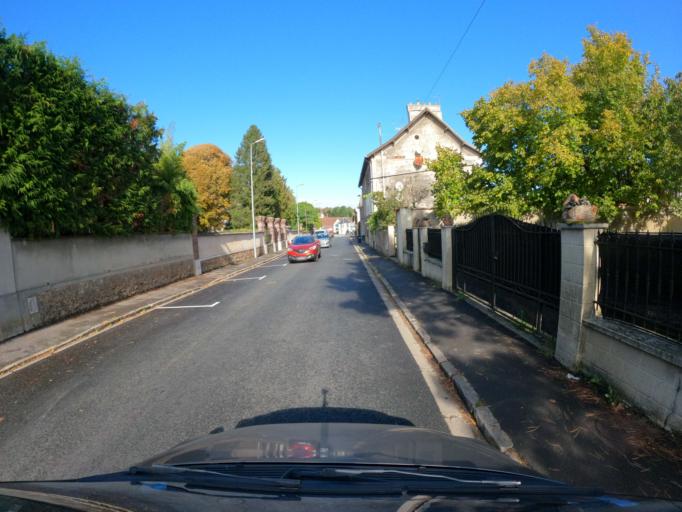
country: FR
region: Ile-de-France
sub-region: Departement de Seine-et-Marne
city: Saint-Germain-sur-Morin
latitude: 48.8816
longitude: 2.8511
